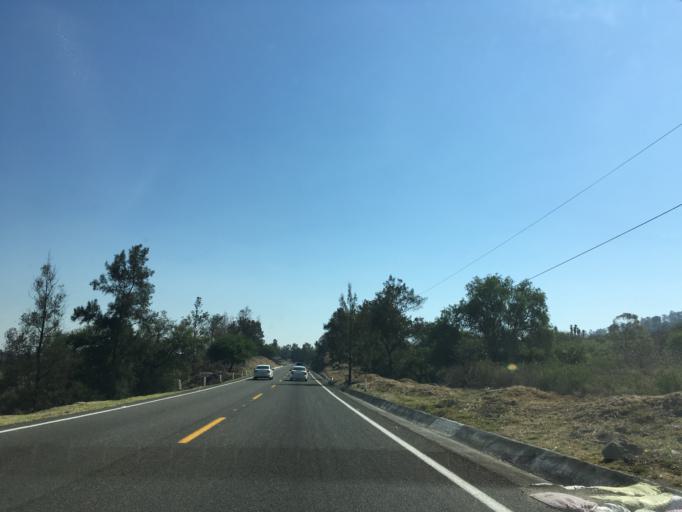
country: MX
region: Michoacan
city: Charo
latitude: 19.7701
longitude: -101.0187
